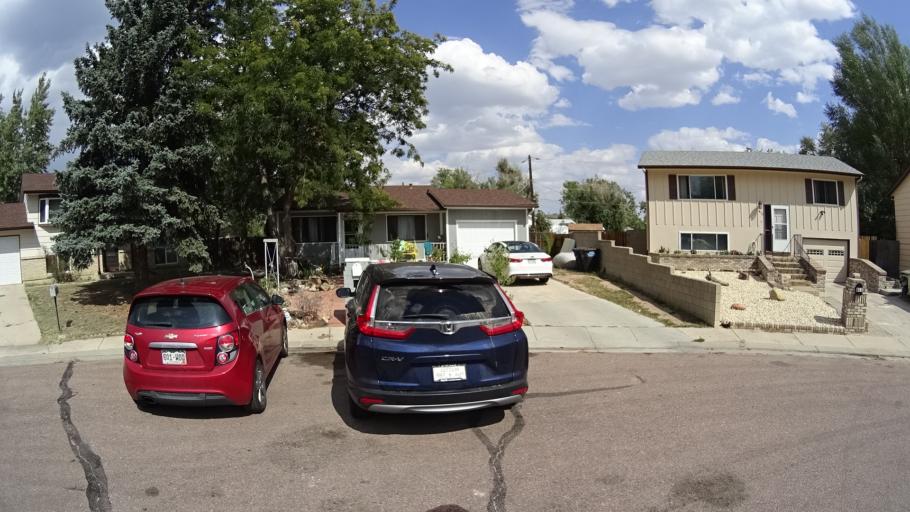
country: US
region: Colorado
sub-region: El Paso County
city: Colorado Springs
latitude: 38.8441
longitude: -104.7717
